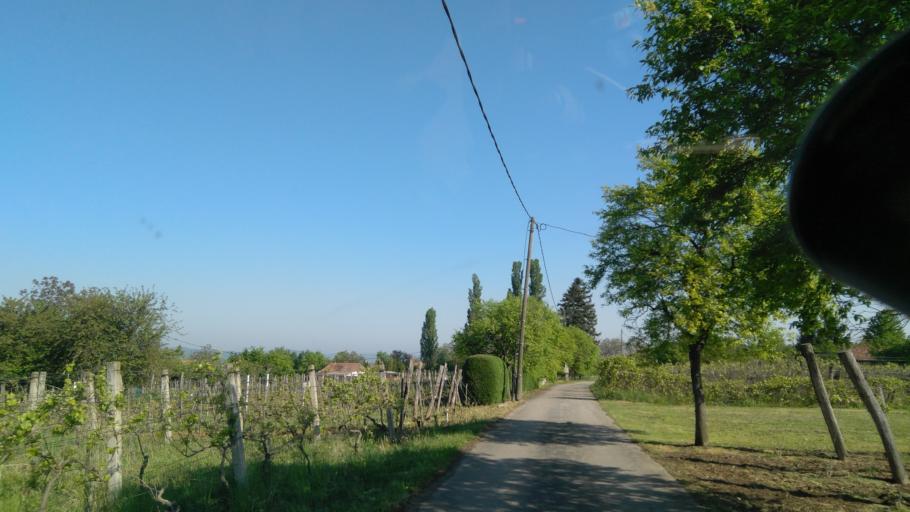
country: HU
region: Zala
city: Sarmellek
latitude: 46.7564
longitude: 17.1416
